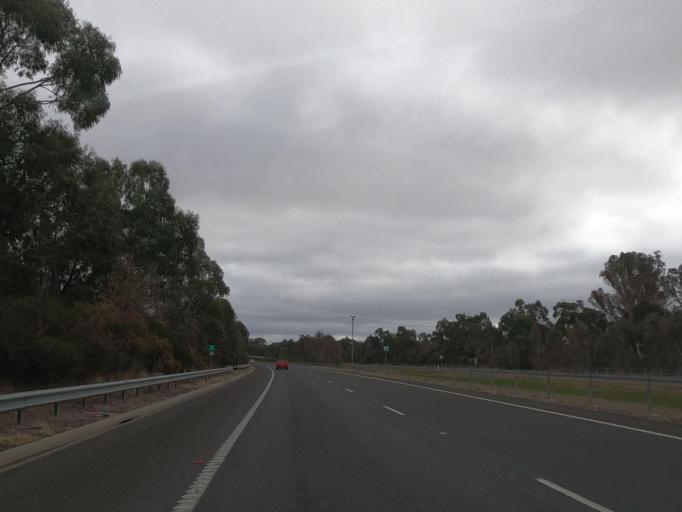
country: AU
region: Victoria
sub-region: Mount Alexander
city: Castlemaine
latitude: -37.0972
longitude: 144.3603
